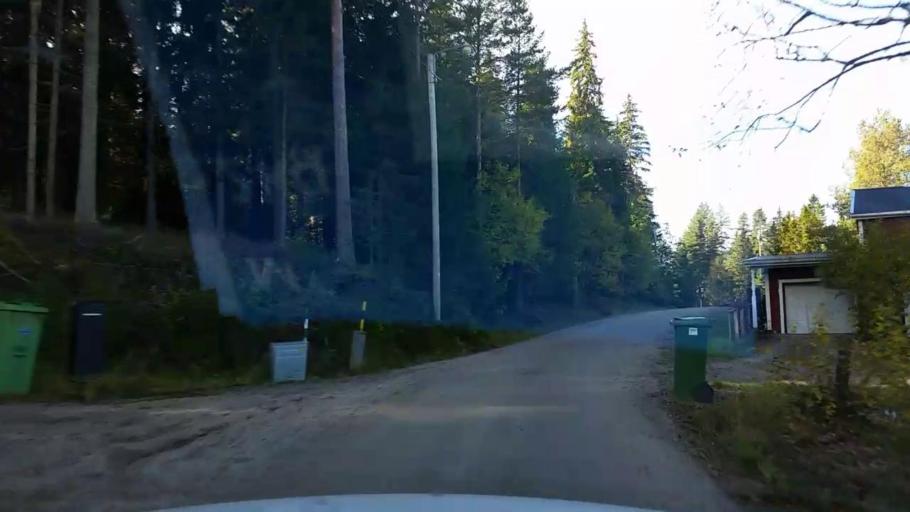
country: SE
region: Gaevleborg
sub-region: Ljusdals Kommun
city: Jaervsoe
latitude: 61.7896
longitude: 16.1965
